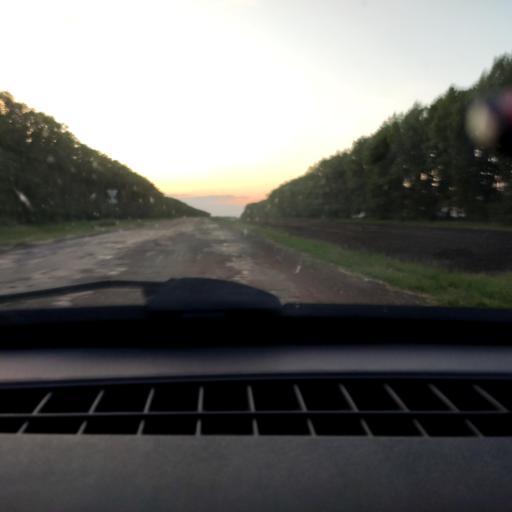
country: RU
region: Bashkortostan
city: Karmaskaly
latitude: 54.3865
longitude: 56.1778
